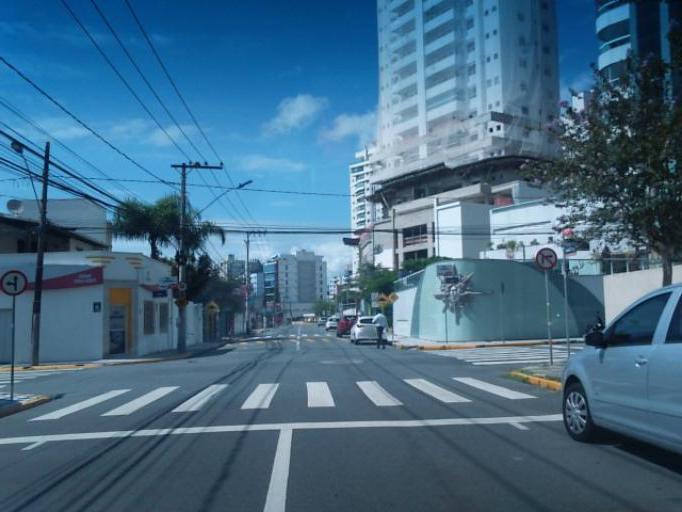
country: BR
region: Santa Catarina
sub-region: Itajai
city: Itajai
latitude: -26.9152
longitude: -48.6538
